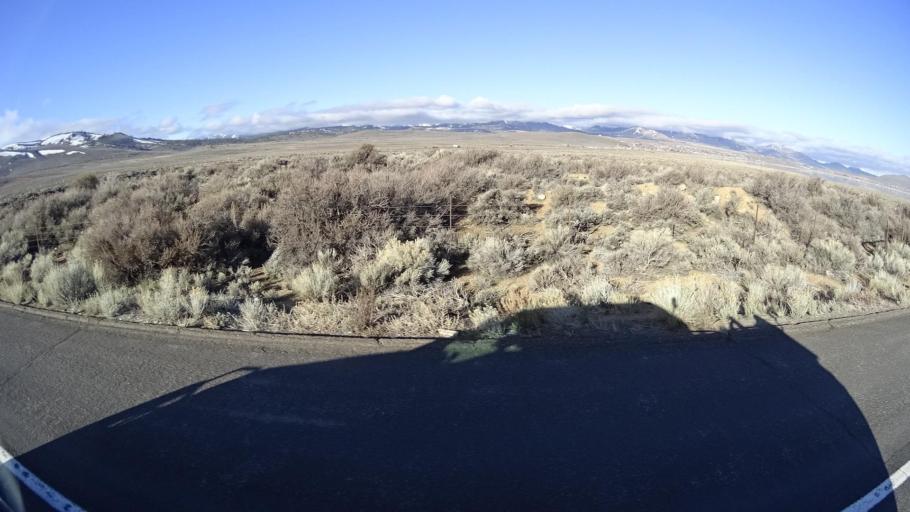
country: US
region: Nevada
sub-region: Washoe County
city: Cold Springs
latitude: 39.6469
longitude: -119.9575
